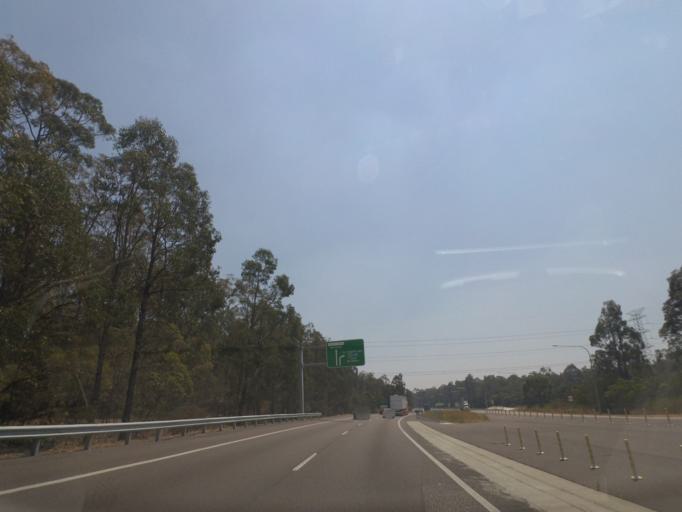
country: AU
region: New South Wales
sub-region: Newcastle
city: Beresfield
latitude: -32.8198
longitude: 151.6343
